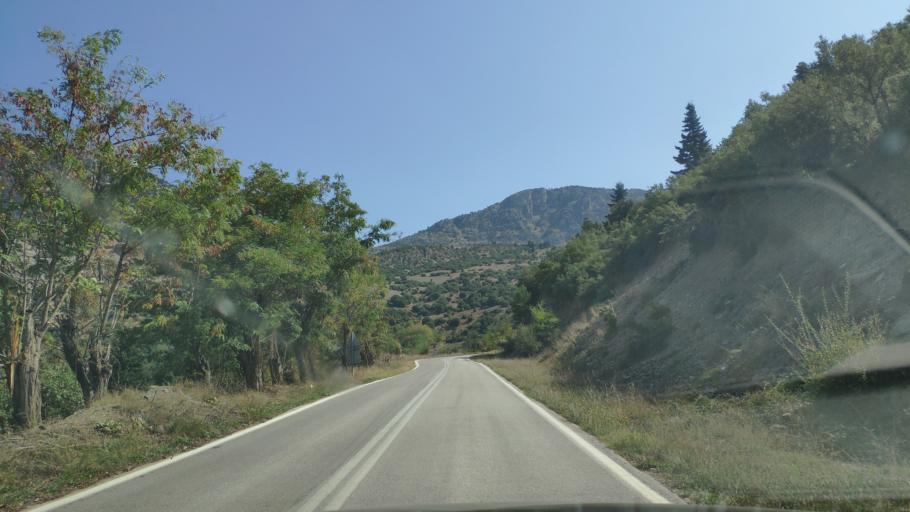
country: GR
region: West Greece
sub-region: Nomos Achaias
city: Aiyira
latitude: 37.9219
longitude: 22.3337
